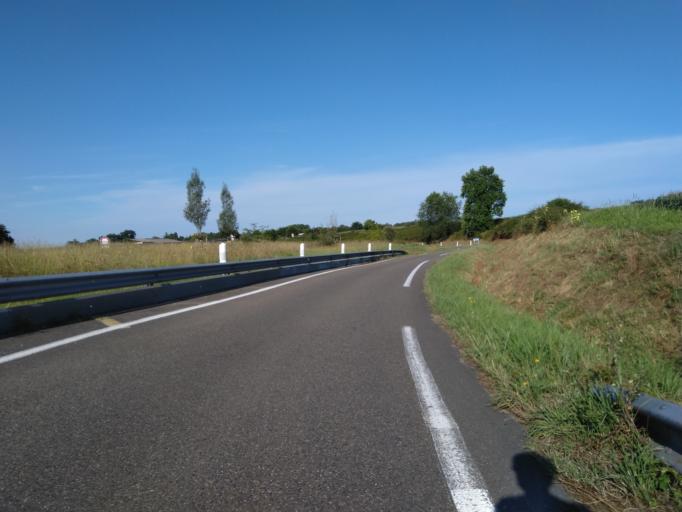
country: FR
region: Aquitaine
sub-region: Departement des Landes
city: Saint-Vincent-de-Paul
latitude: 43.7377
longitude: -1.0239
